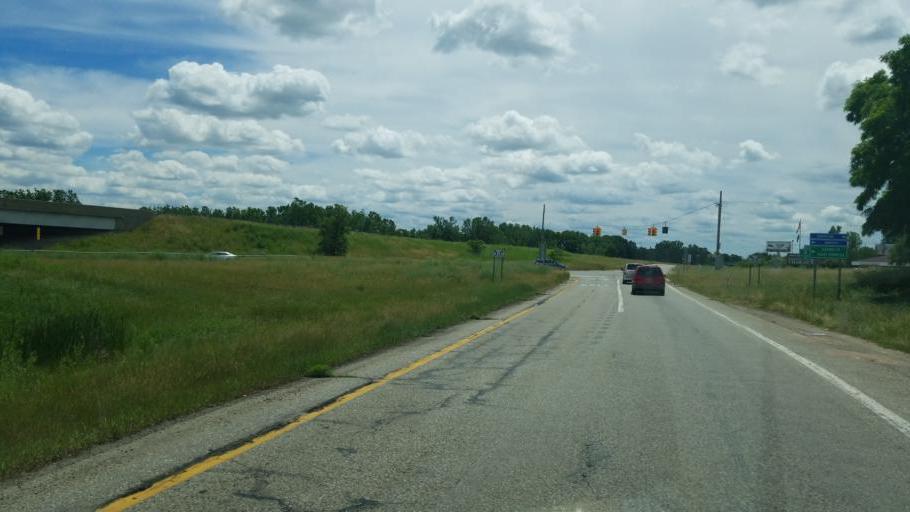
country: US
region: Michigan
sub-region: Eaton County
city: Charlotte
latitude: 42.5755
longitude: -84.8210
